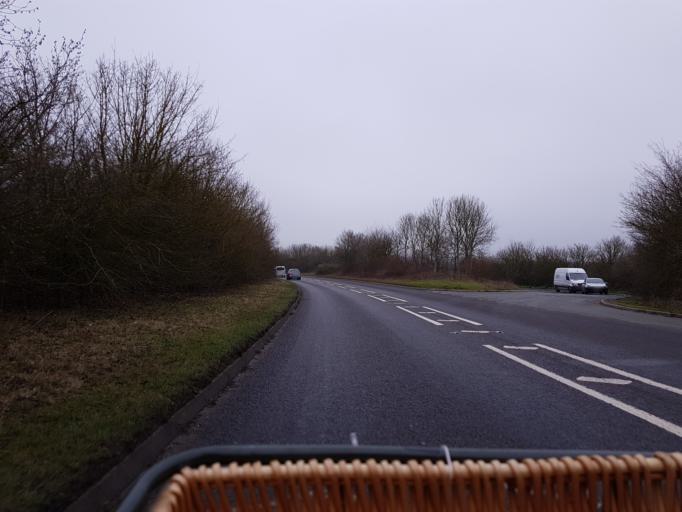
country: GB
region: England
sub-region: Cambridgeshire
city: Duxford
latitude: 52.0714
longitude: 0.1920
